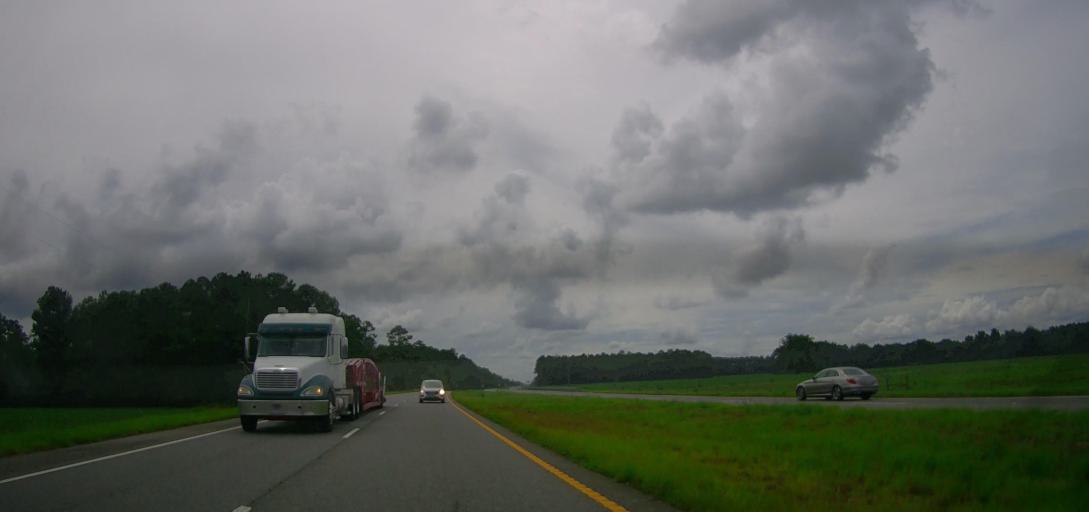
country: US
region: Georgia
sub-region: Wayne County
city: Jesup
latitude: 31.6684
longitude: -82.0480
